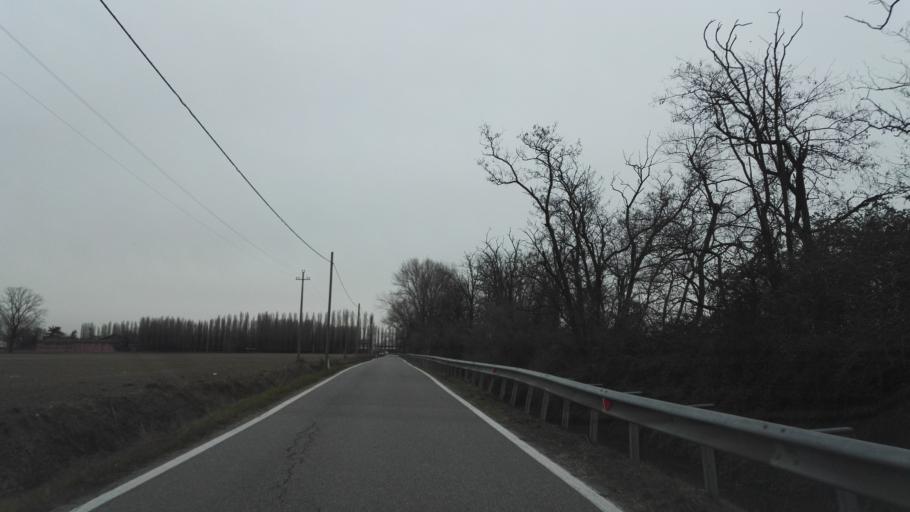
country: IT
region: Lombardy
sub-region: Citta metropolitana di Milano
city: Bettola-Zeloforomagno
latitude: 45.4414
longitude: 9.3171
